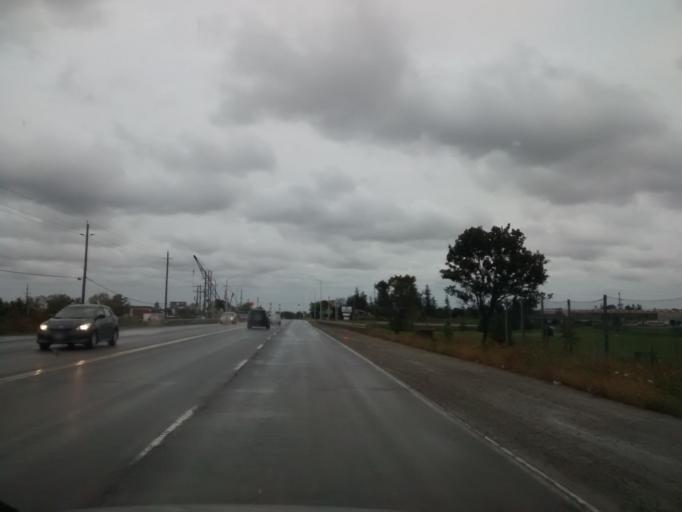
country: CA
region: Ontario
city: Hamilton
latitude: 43.1970
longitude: -79.7662
